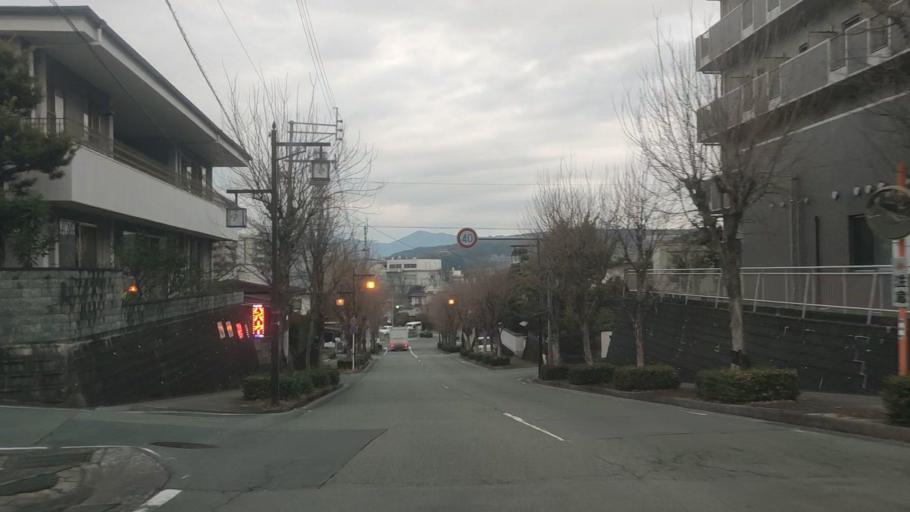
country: JP
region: Kumamoto
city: Kumamoto
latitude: 32.8152
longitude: 130.7550
